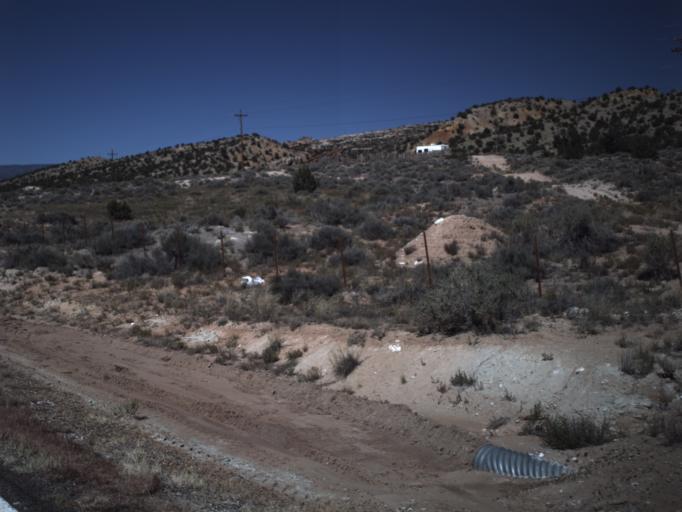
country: US
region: Utah
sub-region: Wayne County
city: Loa
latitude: 37.7434
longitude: -111.5599
